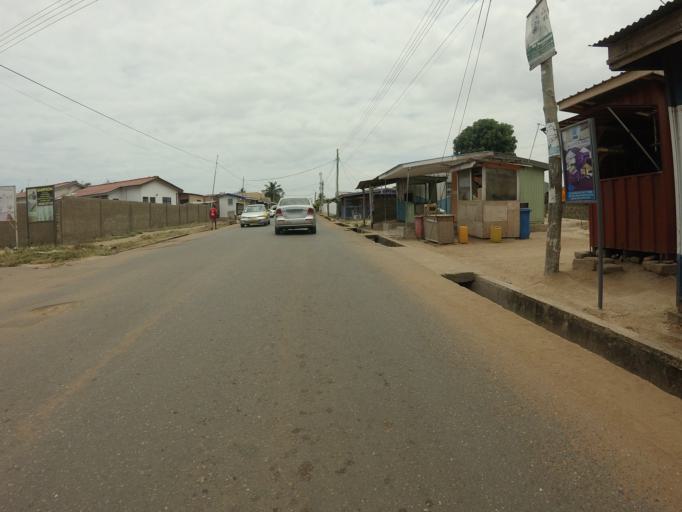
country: GH
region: Greater Accra
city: Nungua
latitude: 5.6059
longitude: -0.0987
